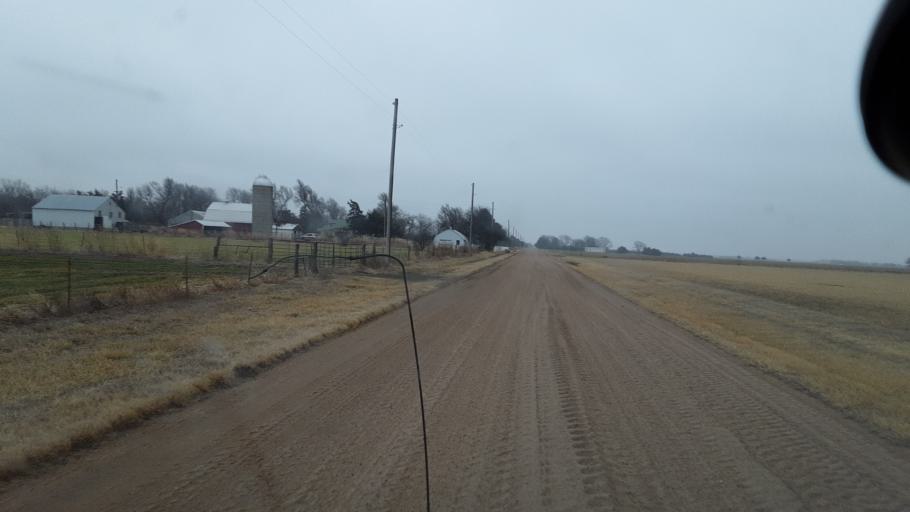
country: US
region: Kansas
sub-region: Reno County
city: South Hutchinson
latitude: 37.9846
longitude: -98.0112
